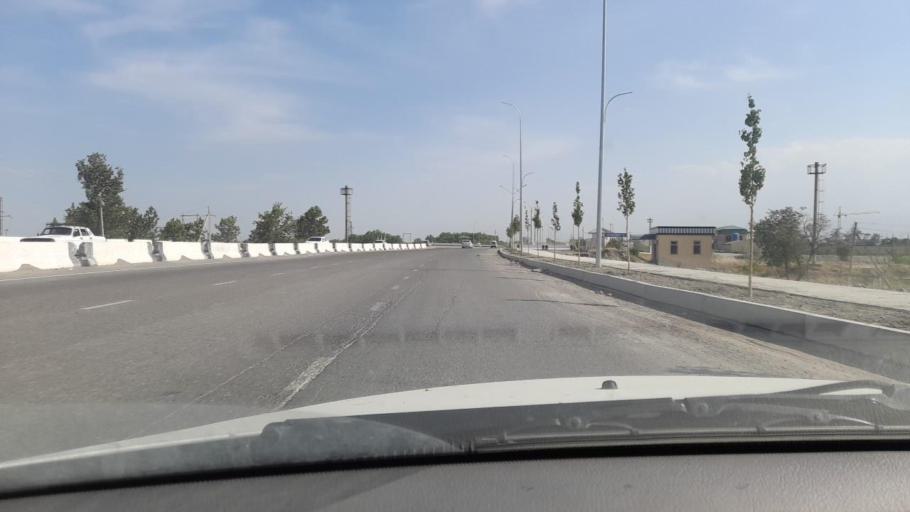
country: UZ
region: Samarqand
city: Daxbet
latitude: 39.7258
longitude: 66.9468
